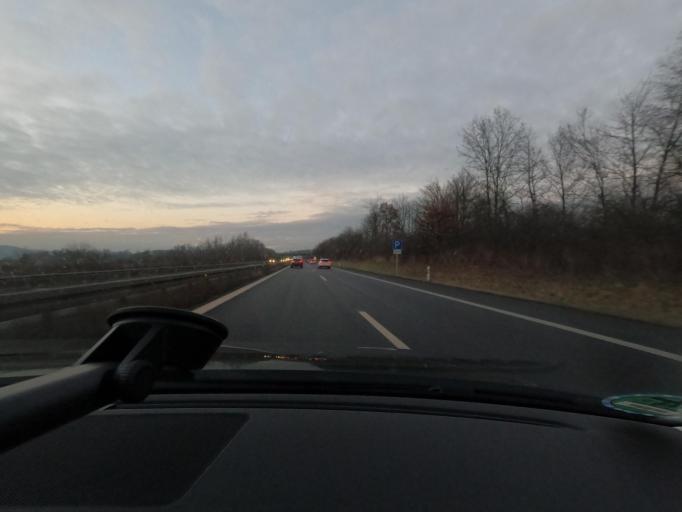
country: DE
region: Bavaria
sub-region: Upper Franconia
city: Gundelsheim
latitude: 49.9380
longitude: 10.9090
